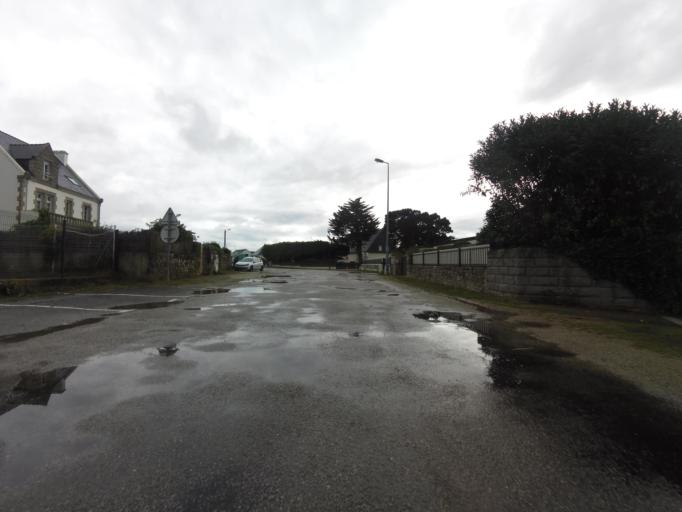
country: FR
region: Brittany
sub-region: Departement du Morbihan
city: Etel
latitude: 47.6625
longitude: -3.2052
